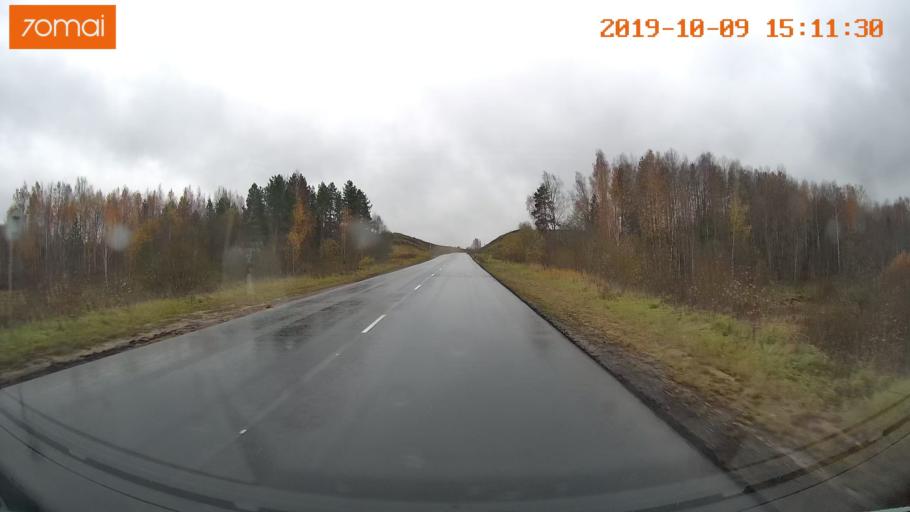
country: RU
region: Kostroma
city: Susanino
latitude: 58.1640
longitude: 41.6296
